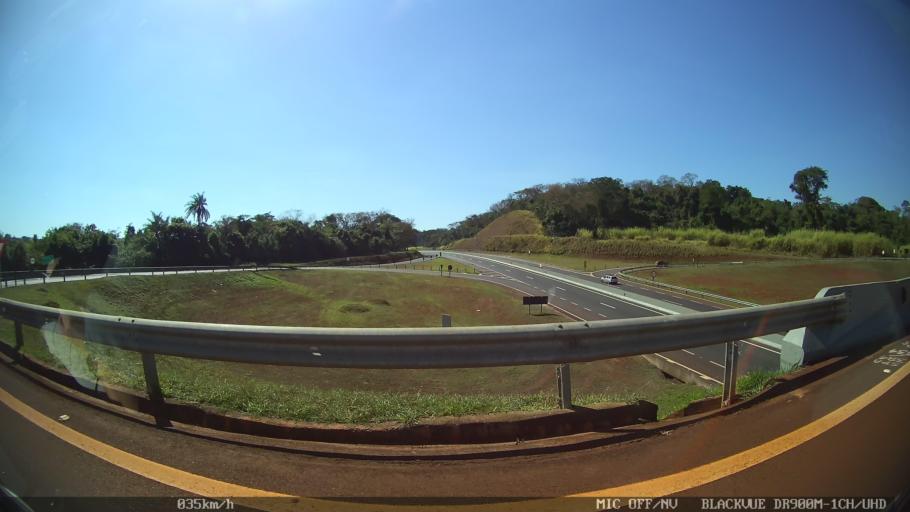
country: BR
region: Sao Paulo
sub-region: Franca
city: Franca
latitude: -20.6343
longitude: -47.4693
